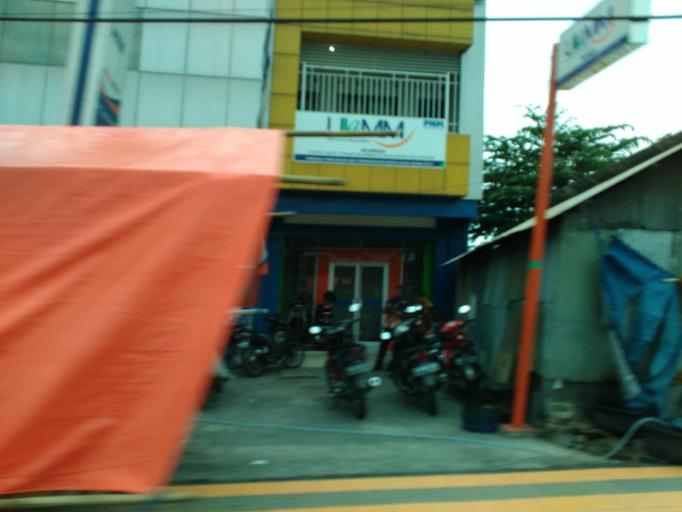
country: ID
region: Central Java
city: Gatak
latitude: -7.5964
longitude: 110.7033
